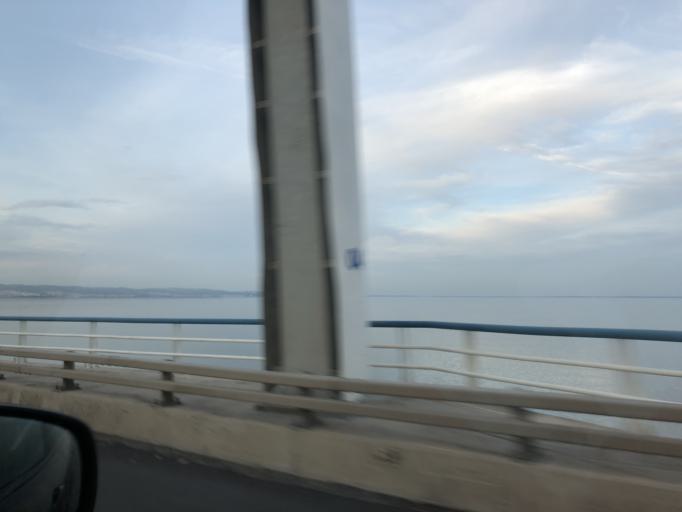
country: PT
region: Lisbon
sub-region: Loures
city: Moscavide
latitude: 38.7623
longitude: -9.0420
